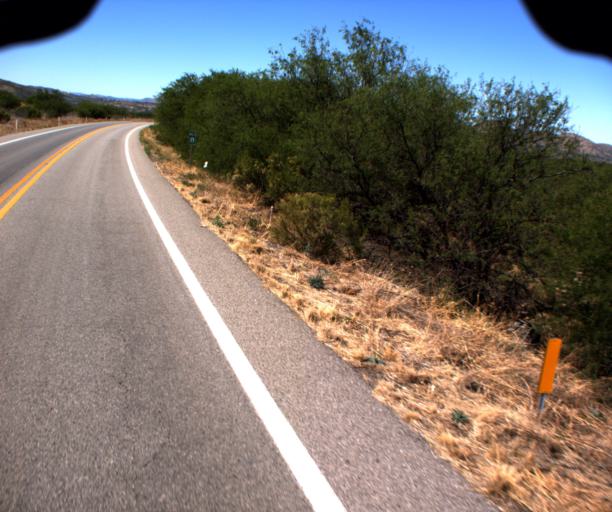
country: US
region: Arizona
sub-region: Santa Cruz County
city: Nogales
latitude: 31.4145
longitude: -110.8551
